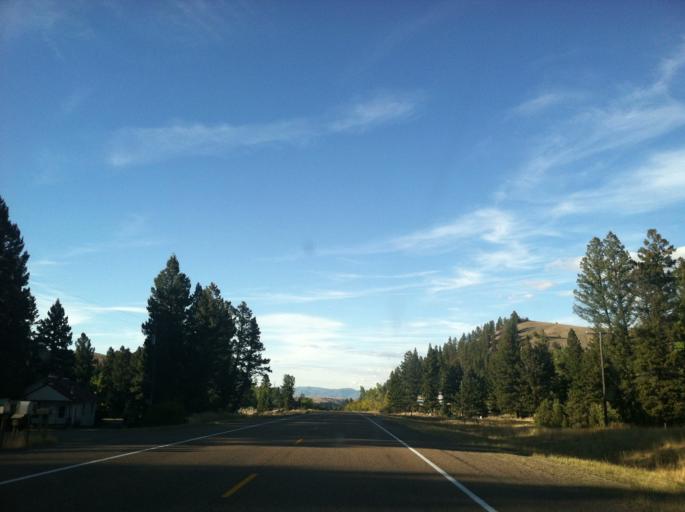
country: US
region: Montana
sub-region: Granite County
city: Philipsburg
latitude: 46.4720
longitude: -113.2346
